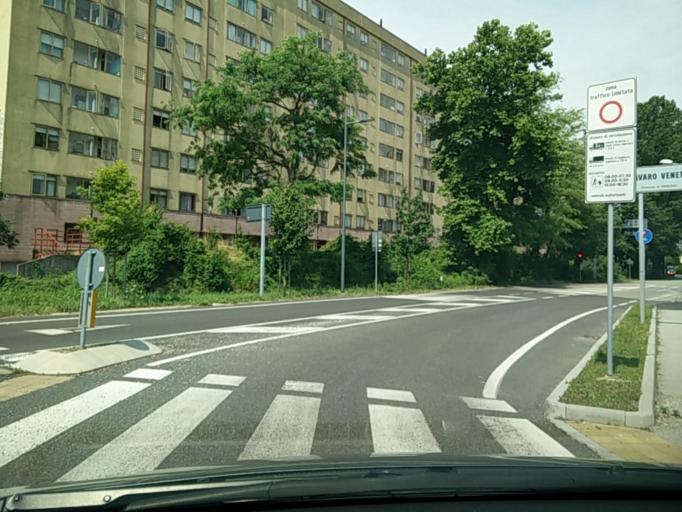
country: IT
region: Veneto
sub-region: Provincia di Venezia
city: Campalto
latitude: 45.5043
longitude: 12.2912
